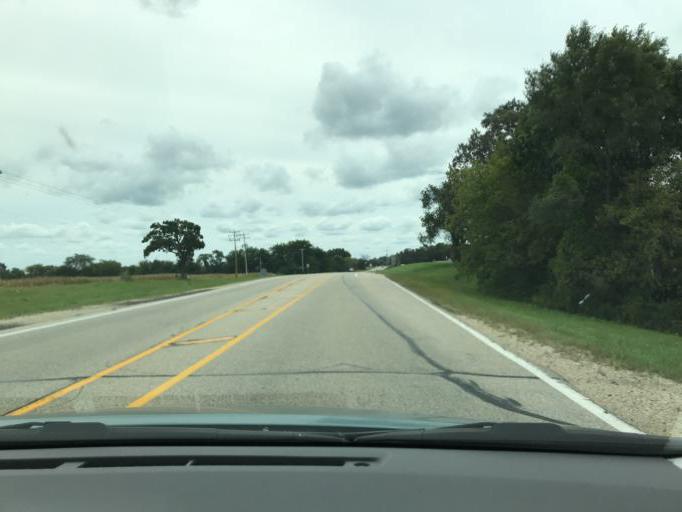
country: US
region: Wisconsin
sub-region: Racine County
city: Bohners Lake
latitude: 42.6423
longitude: -88.2510
